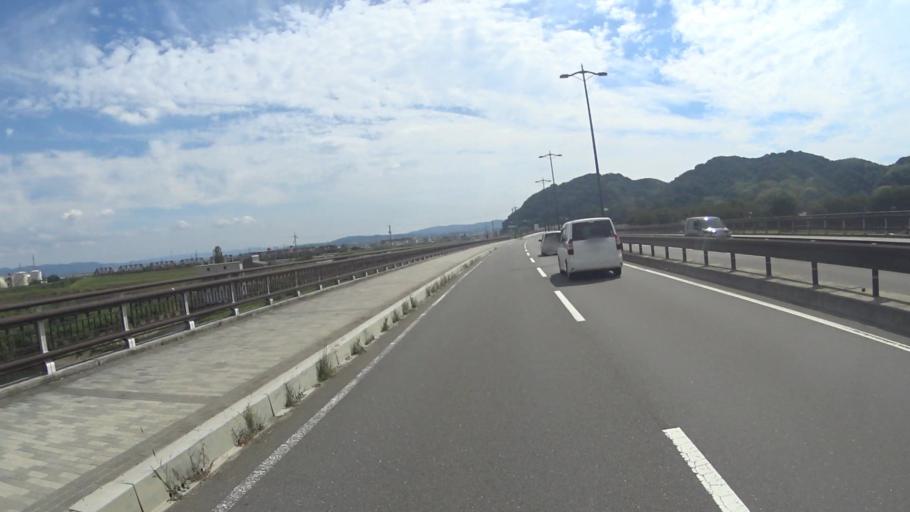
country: JP
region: Kyoto
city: Yawata
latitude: 34.8925
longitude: 135.7009
